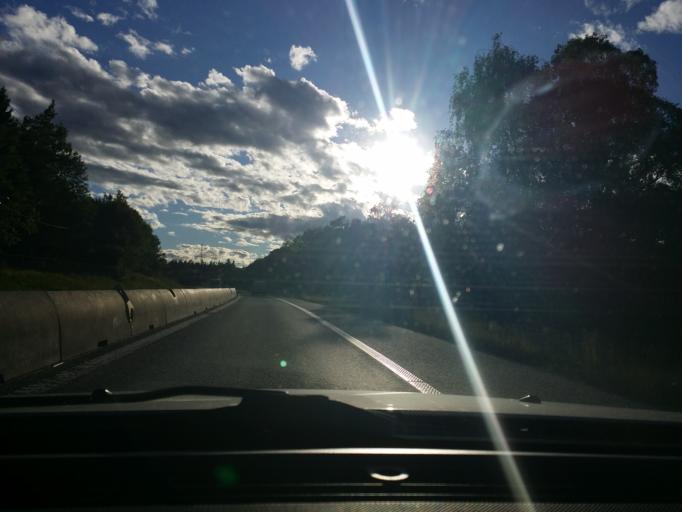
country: SE
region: Stockholm
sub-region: Upplands Vasby Kommun
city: Upplands Vaesby
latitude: 59.4747
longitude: 17.8888
